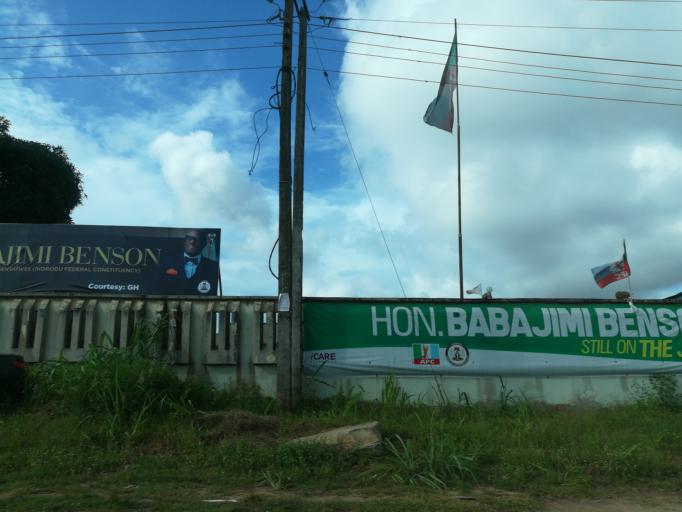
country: NG
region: Lagos
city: Ebute Ikorodu
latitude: 6.5969
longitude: 3.5014
